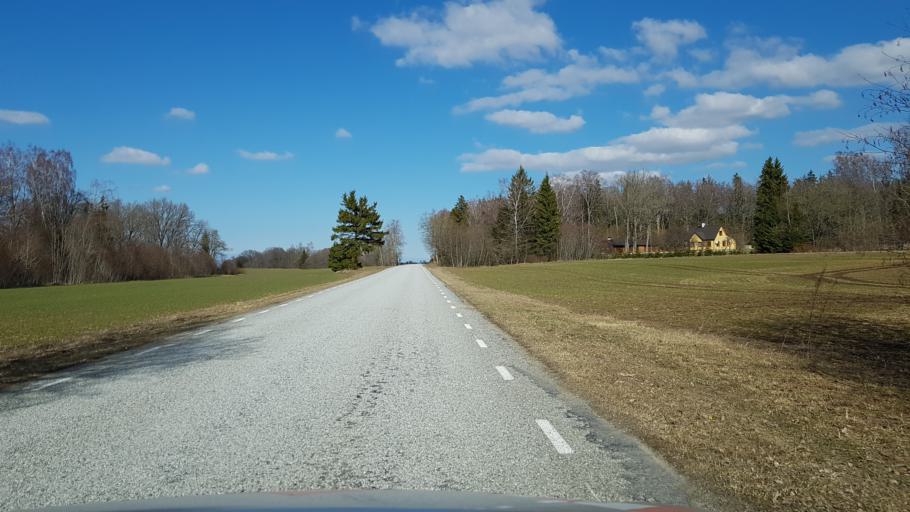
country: EE
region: Laeaene-Virumaa
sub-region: Kadrina vald
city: Kadrina
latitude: 59.3050
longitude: 26.2255
